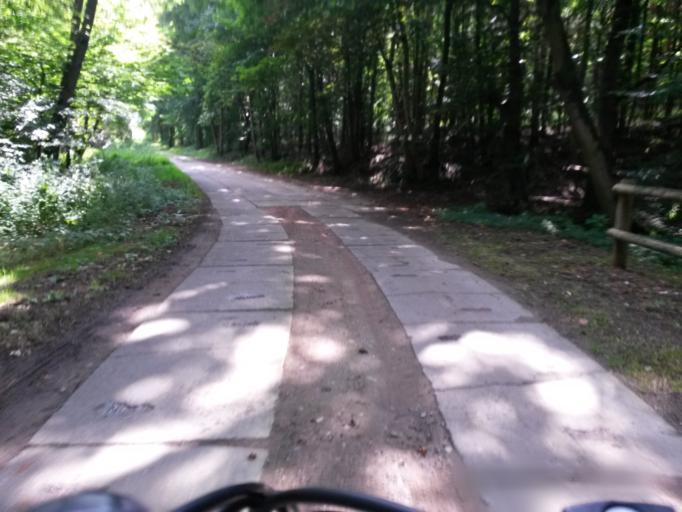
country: DE
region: Brandenburg
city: Althuttendorf
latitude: 53.0137
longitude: 13.8685
